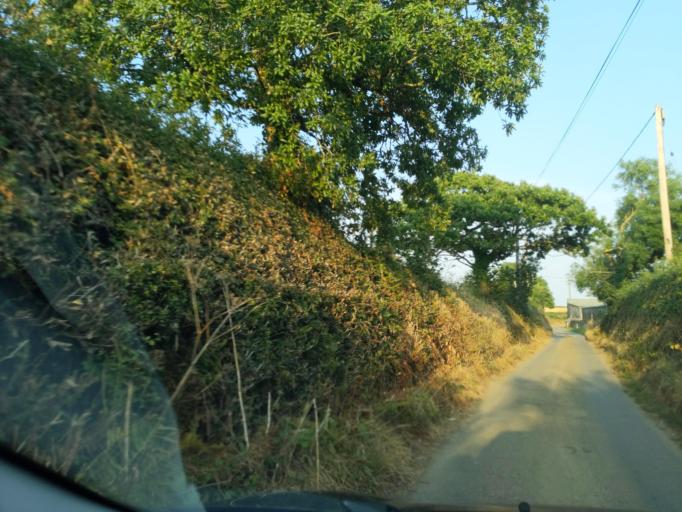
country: GB
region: England
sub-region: Cornwall
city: Fowey
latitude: 50.3685
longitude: -4.5931
